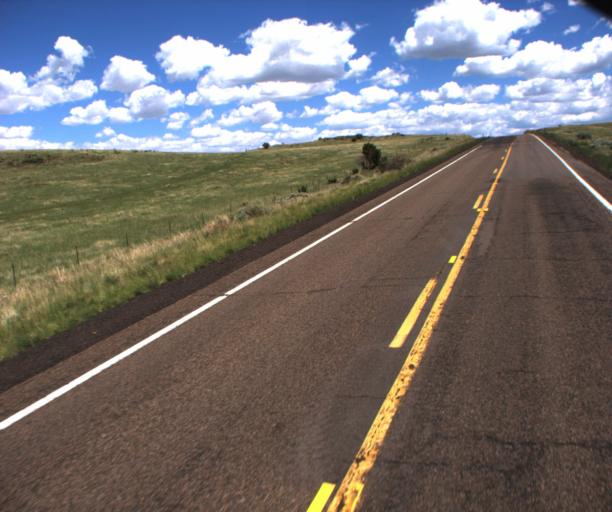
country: US
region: Arizona
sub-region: Apache County
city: Springerville
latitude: 34.2138
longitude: -109.4528
